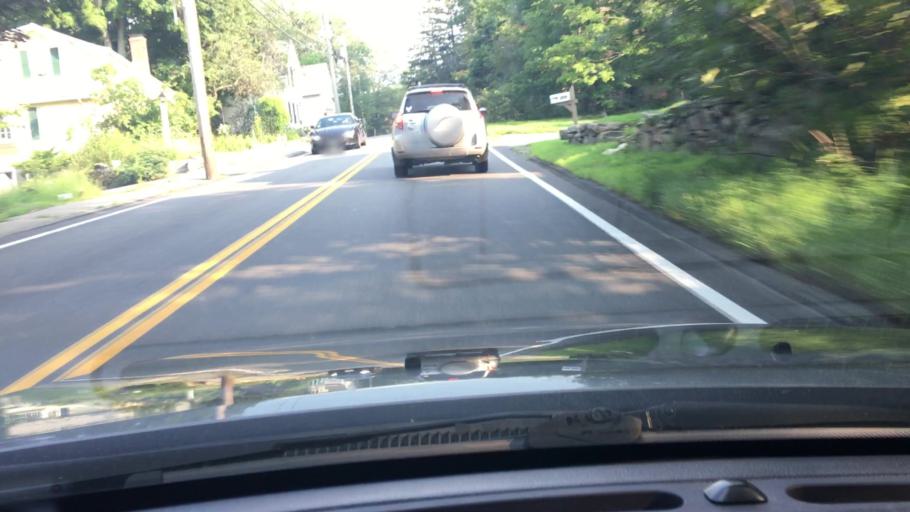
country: US
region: Massachusetts
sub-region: Middlesex County
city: Hopkinton
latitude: 42.2398
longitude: -71.5663
